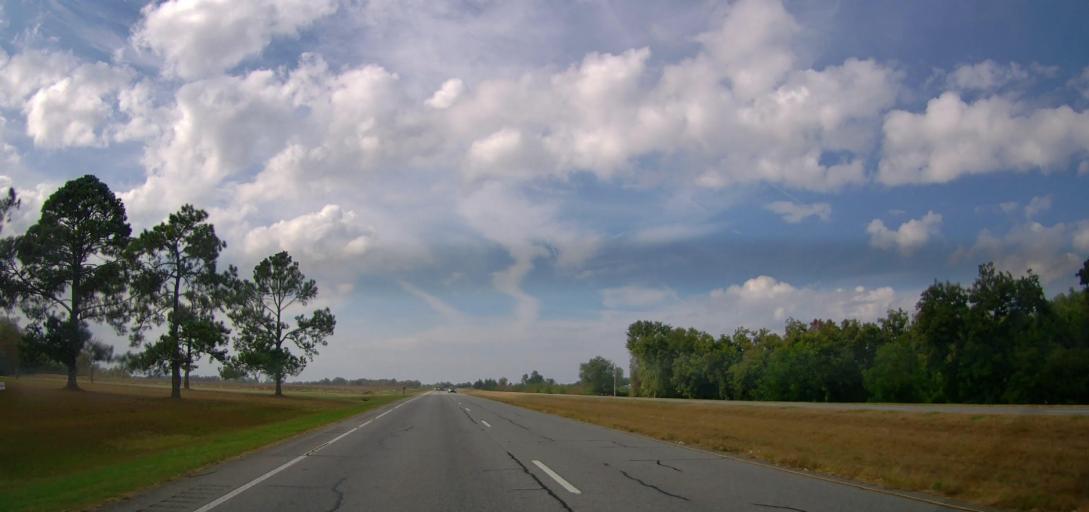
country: US
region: Georgia
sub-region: Mitchell County
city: Pelham
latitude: 31.1076
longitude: -84.1159
